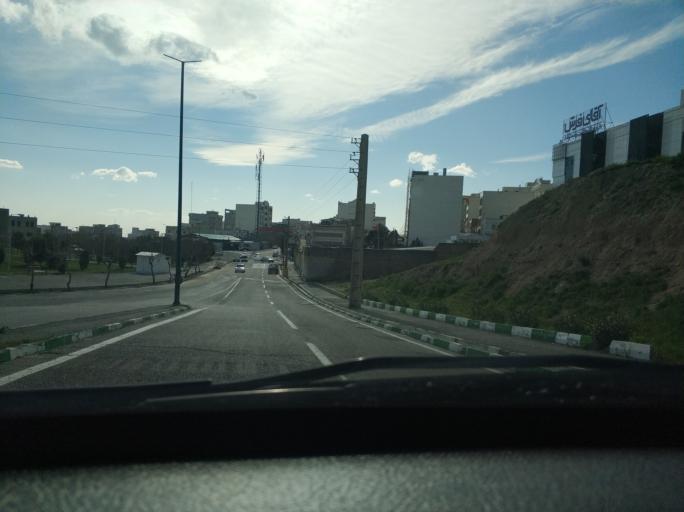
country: IR
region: Tehran
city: Tajrish
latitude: 35.7435
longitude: 51.5962
